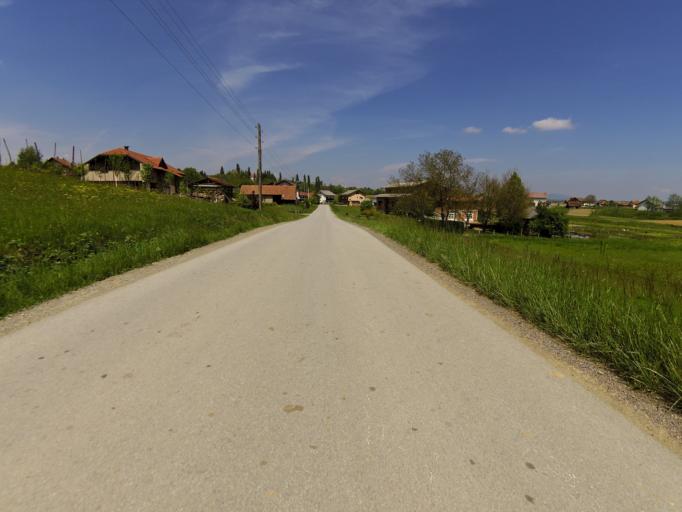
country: HR
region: Karlovacka
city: Ozalj
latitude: 45.5603
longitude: 15.4794
